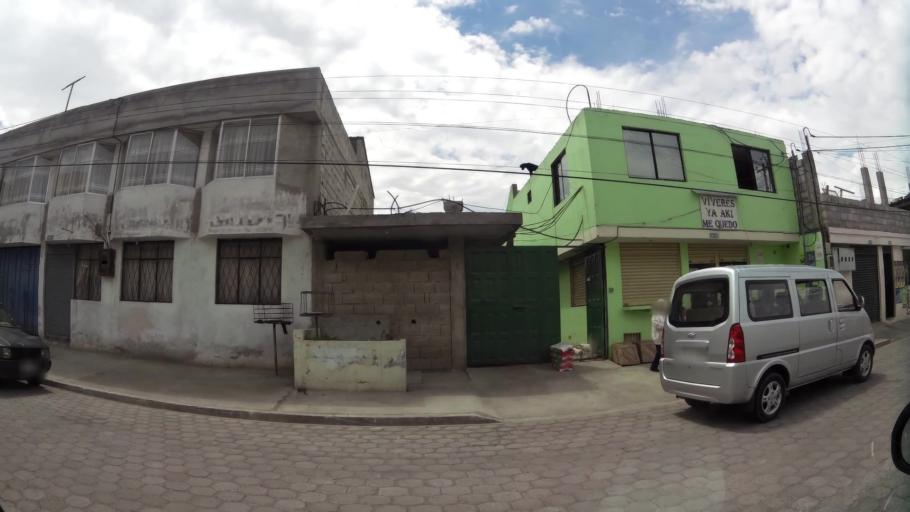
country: EC
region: Pichincha
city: Quito
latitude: -0.0817
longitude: -78.4139
